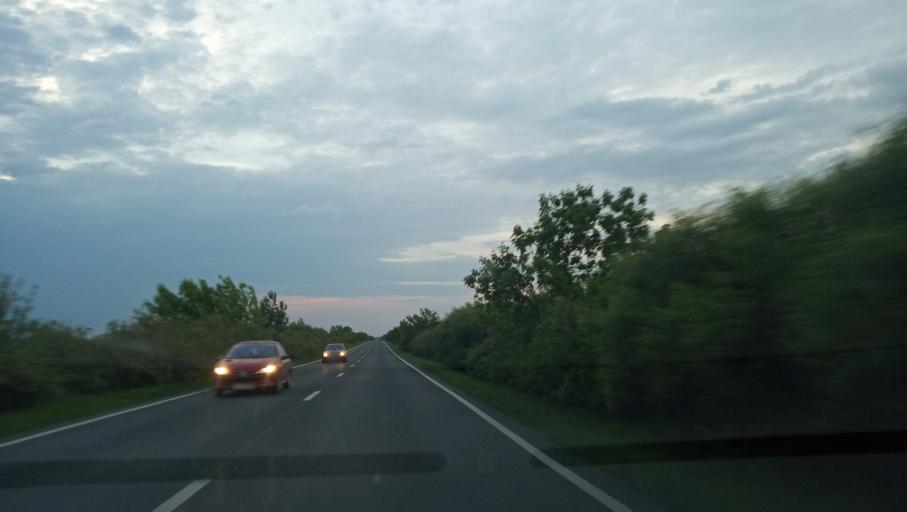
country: RO
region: Timis
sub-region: Comuna Jebel
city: Jebel
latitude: 45.5233
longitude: 21.2324
